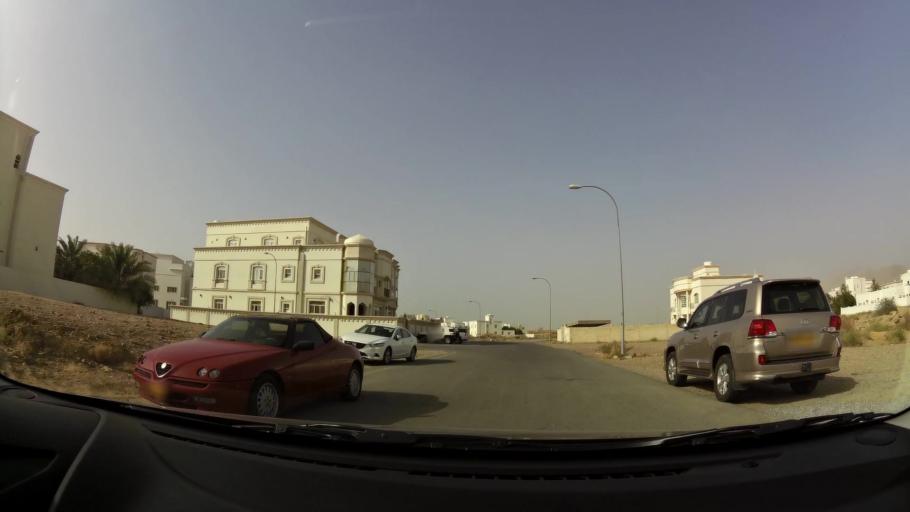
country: OM
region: Muhafazat Masqat
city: Bawshar
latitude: 23.5498
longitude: 58.3626
